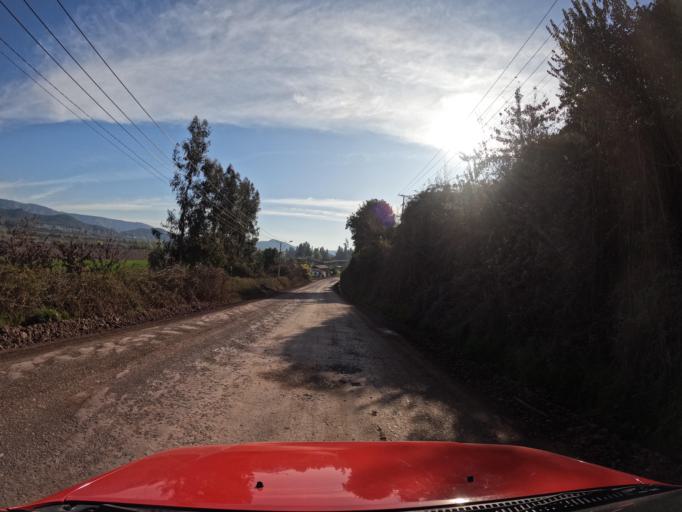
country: CL
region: Maule
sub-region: Provincia de Curico
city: Teno
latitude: -34.9699
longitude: -70.9357
